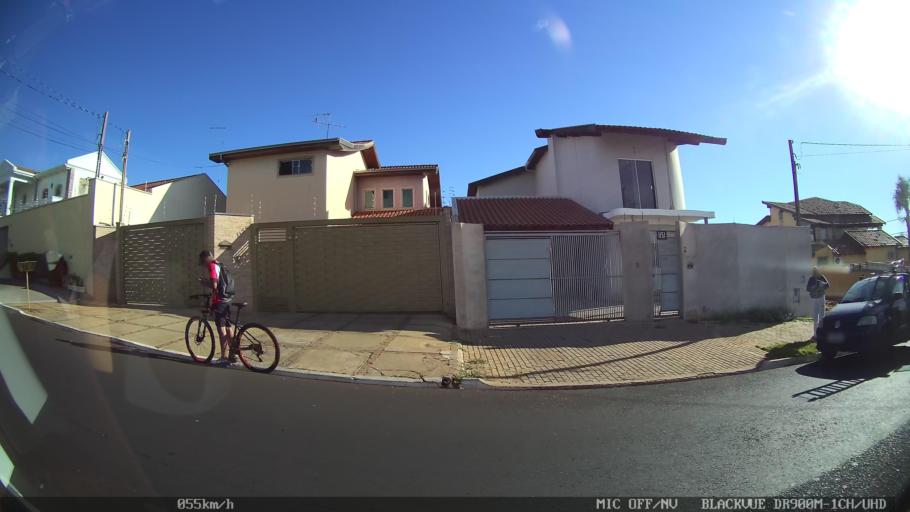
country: BR
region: Sao Paulo
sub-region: Araraquara
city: Araraquara
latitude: -21.7624
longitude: -48.1753
